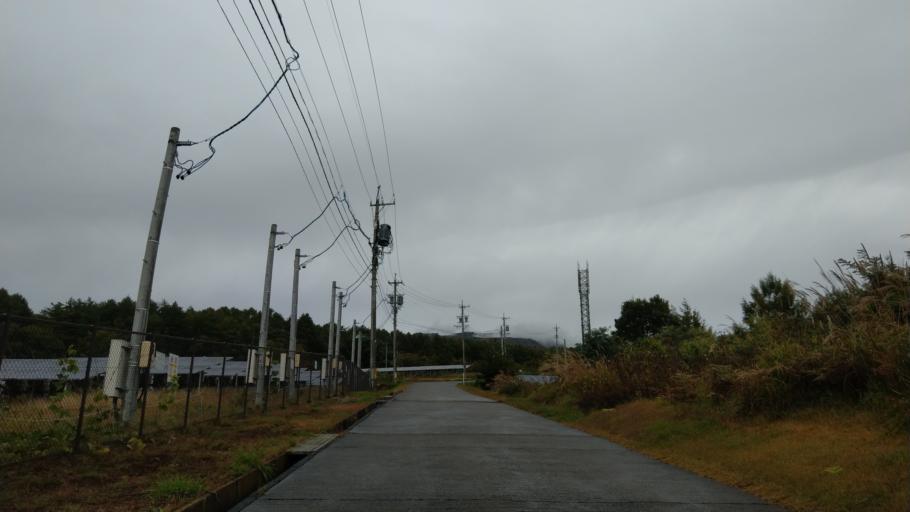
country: JP
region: Nagano
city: Komoro
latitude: 36.3610
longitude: 138.4254
